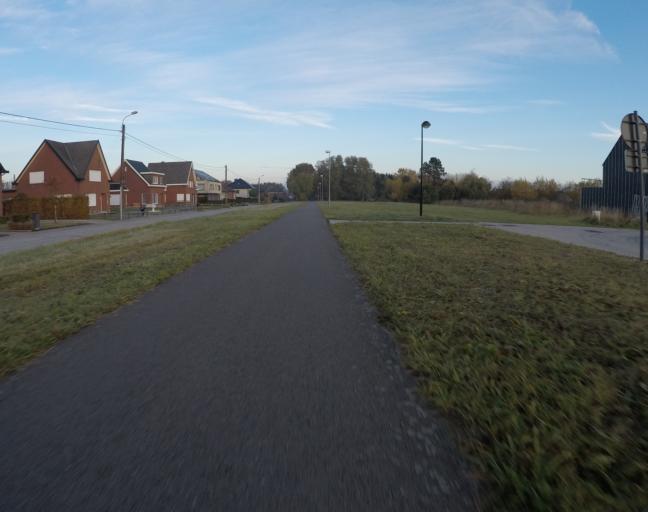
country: BE
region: Flanders
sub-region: Provincie Vlaams-Brabant
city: Begijnendijk
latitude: 51.0326
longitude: 4.8258
